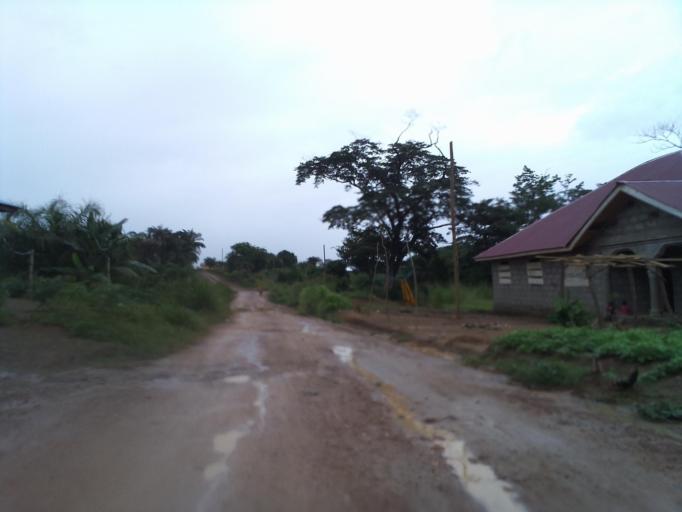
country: SL
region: Eastern Province
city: Kenema
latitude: 7.8773
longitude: -11.1583
